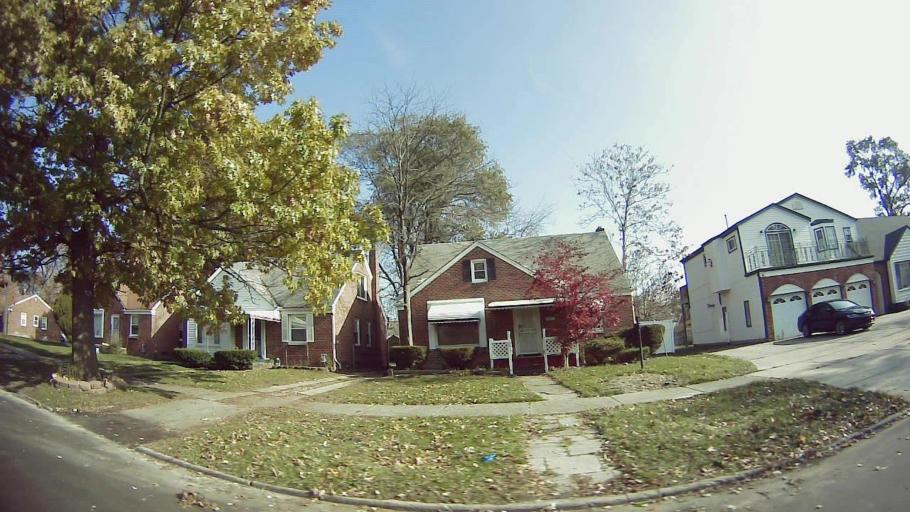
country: US
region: Michigan
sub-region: Oakland County
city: Oak Park
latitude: 42.4415
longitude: -83.1905
